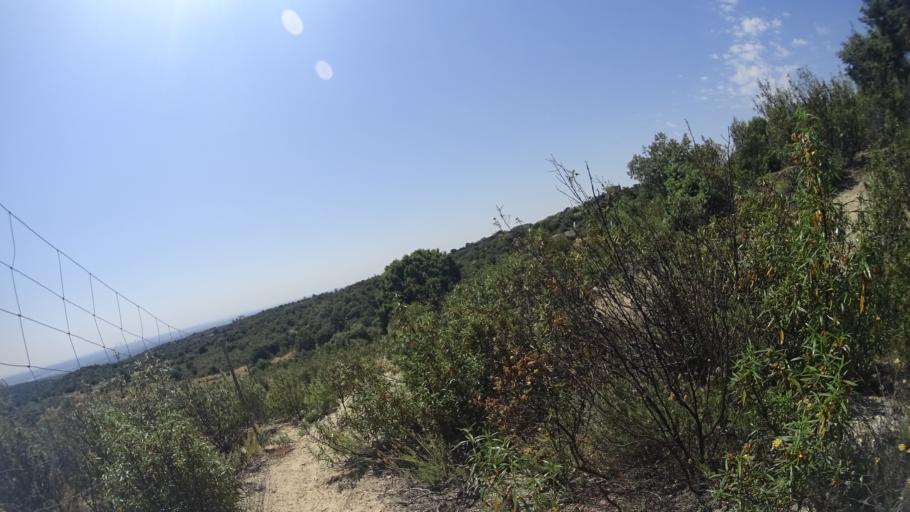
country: ES
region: Madrid
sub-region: Provincia de Madrid
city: Torrelodones
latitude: 40.5974
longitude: -3.9224
